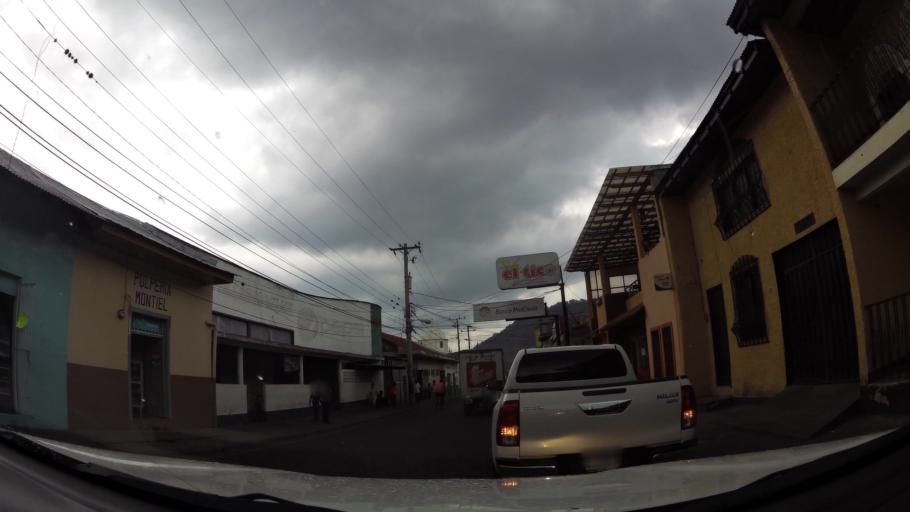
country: NI
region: Jinotega
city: Jinotega
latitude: 13.0909
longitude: -86.0019
